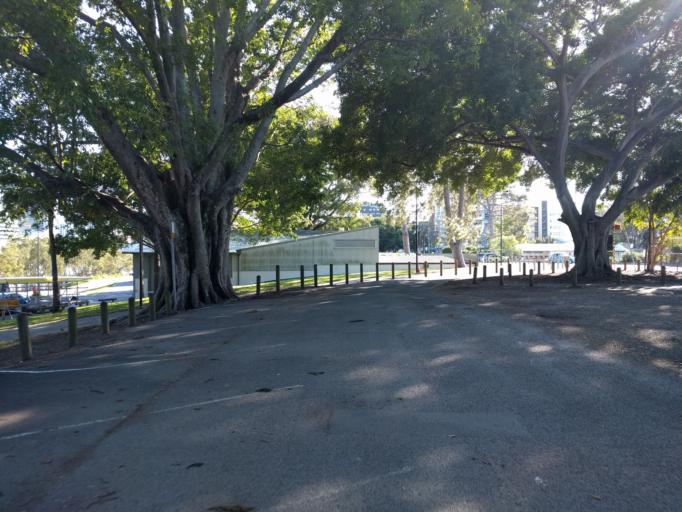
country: AU
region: Queensland
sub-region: Brisbane
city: Milton
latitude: -27.4784
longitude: 153.0038
